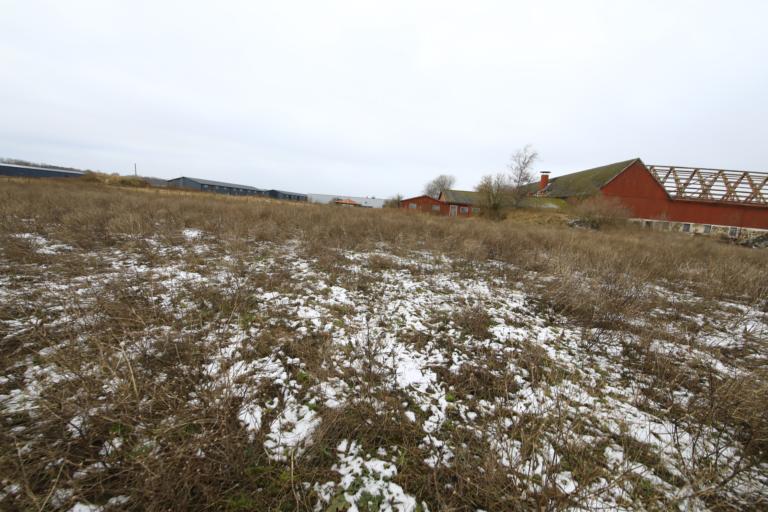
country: SE
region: Halland
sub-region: Varbergs Kommun
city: Varberg
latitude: 57.1234
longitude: 12.3045
